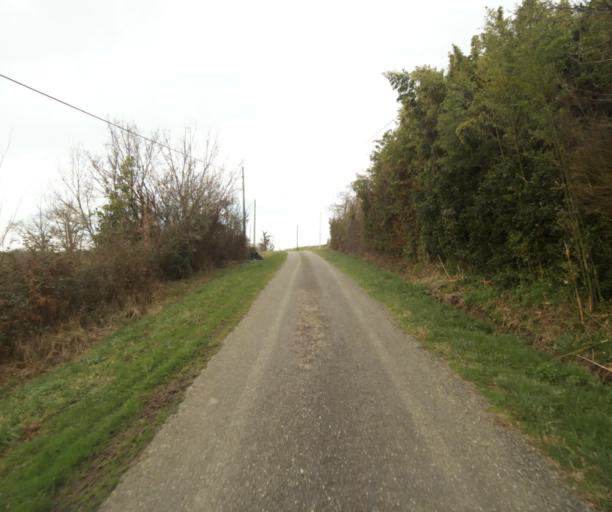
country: FR
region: Midi-Pyrenees
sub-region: Departement du Gers
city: Eauze
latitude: 43.9139
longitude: 0.0475
